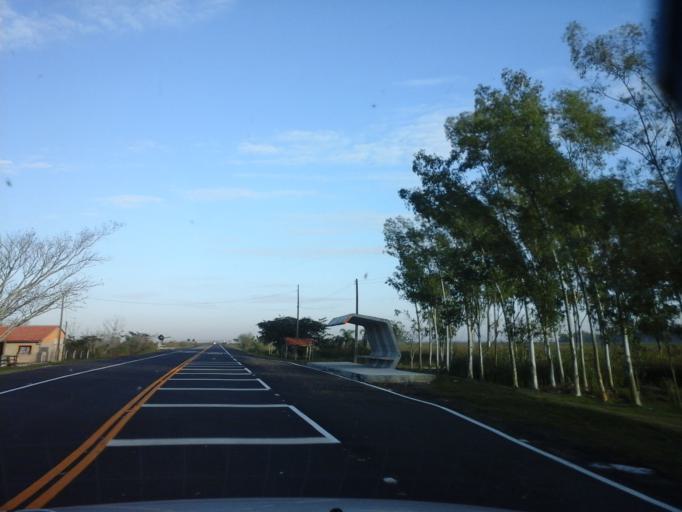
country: PY
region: Neembucu
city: Cerrito
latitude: -26.8940
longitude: -57.6952
